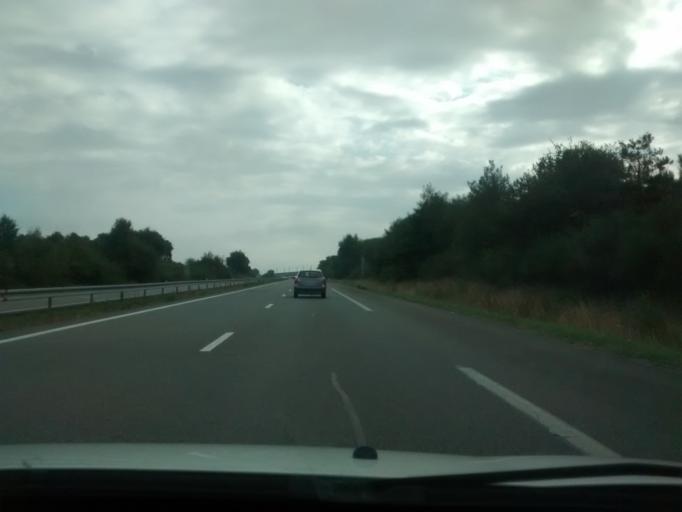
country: FR
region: Pays de la Loire
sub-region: Departement de la Mayenne
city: Loiron
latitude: 48.0805
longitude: -0.8986
